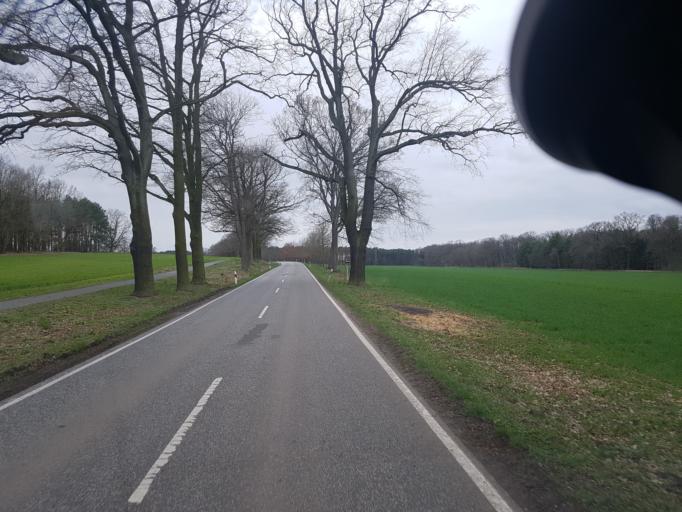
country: DE
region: Brandenburg
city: Mixdorf
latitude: 52.1960
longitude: 14.3377
